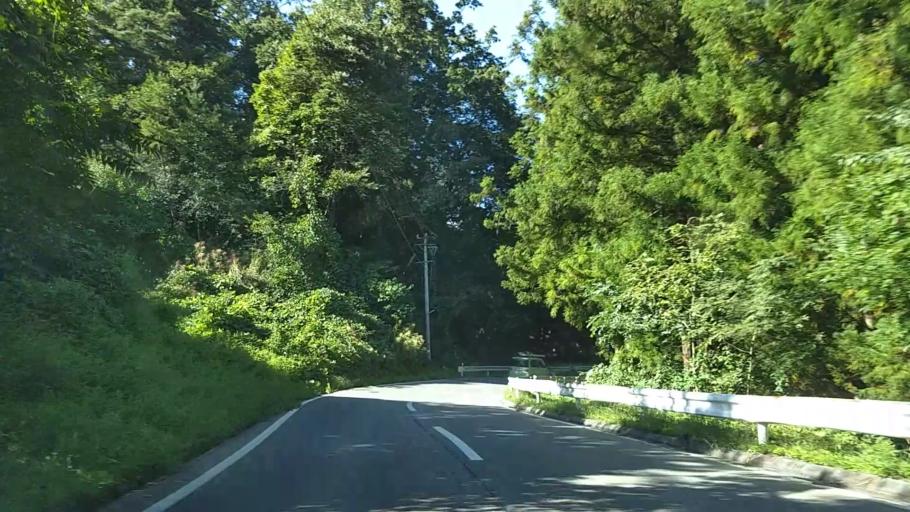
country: JP
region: Nagano
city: Nagano-shi
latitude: 36.6020
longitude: 138.0942
